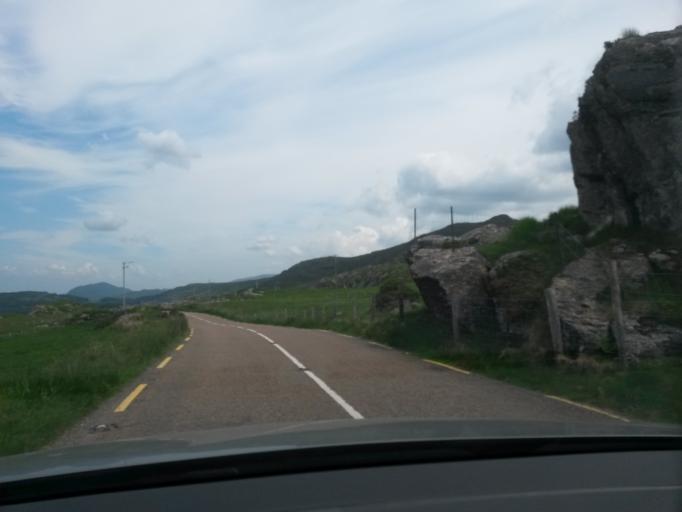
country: IE
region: Munster
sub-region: Ciarrai
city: Kenmare
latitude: 51.9384
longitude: -9.6654
